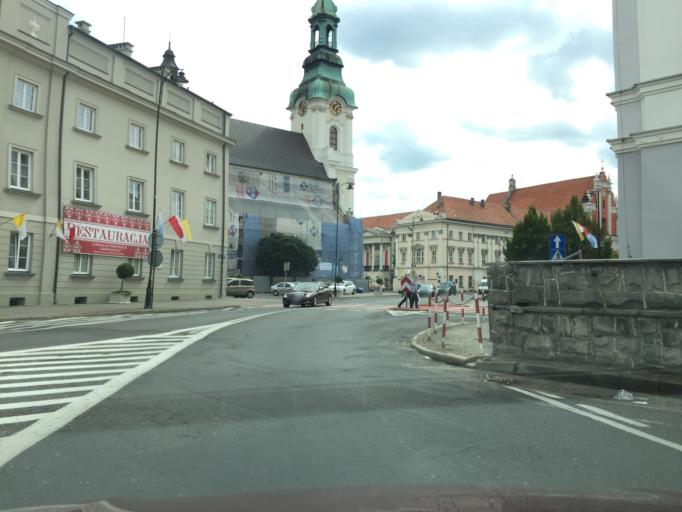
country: PL
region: Greater Poland Voivodeship
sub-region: Kalisz
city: Kalisz
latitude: 51.7642
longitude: 18.0927
